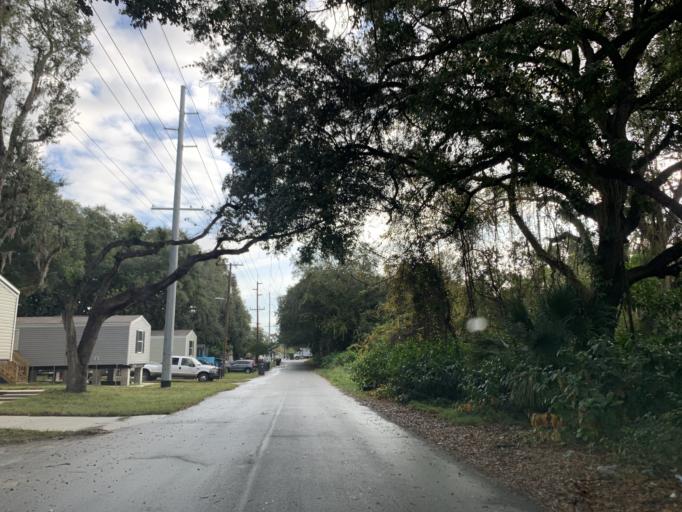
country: US
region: Florida
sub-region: Hillsborough County
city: Mango
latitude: 27.9851
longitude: -82.3206
